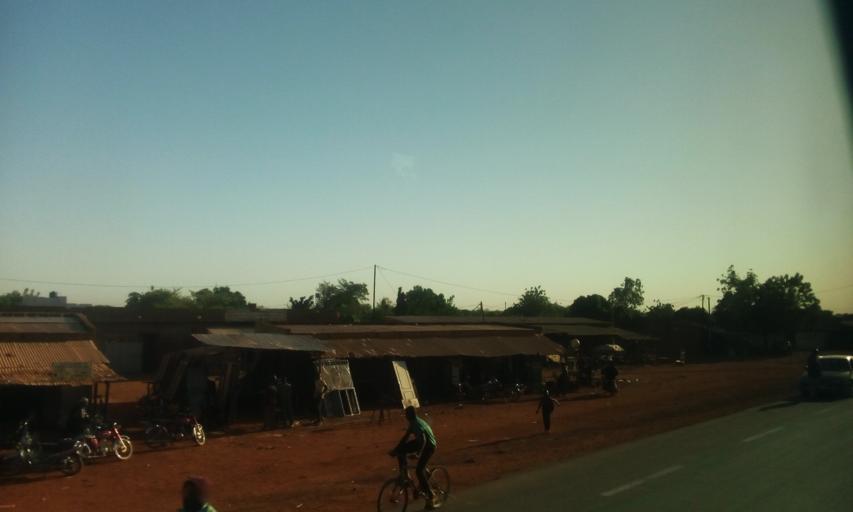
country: ML
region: Segou
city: Baroueli
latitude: 12.7860
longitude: -6.9464
